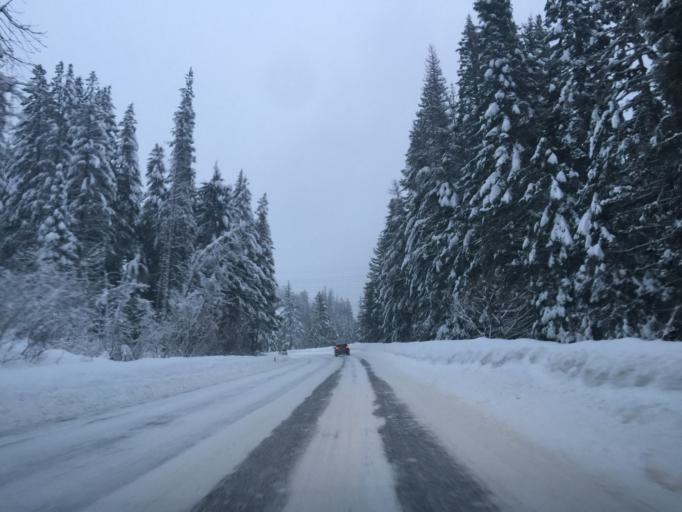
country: US
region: Washington
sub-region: Chelan County
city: Leavenworth
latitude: 47.7818
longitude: -120.9379
